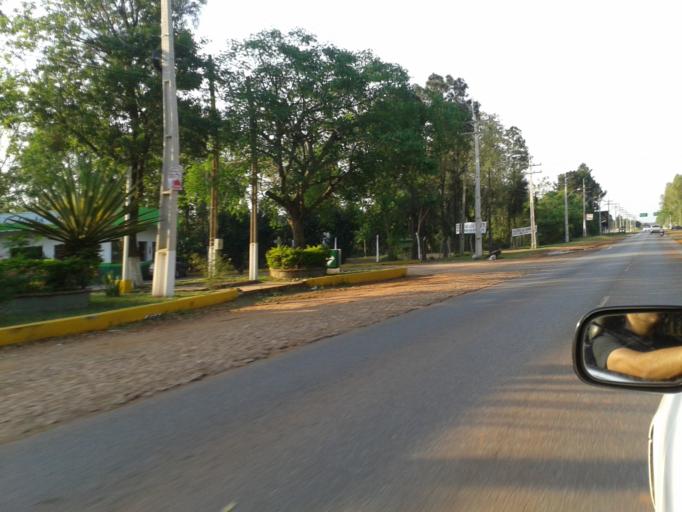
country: PY
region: Guaira
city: Villarrica
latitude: -25.7605
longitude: -56.4389
